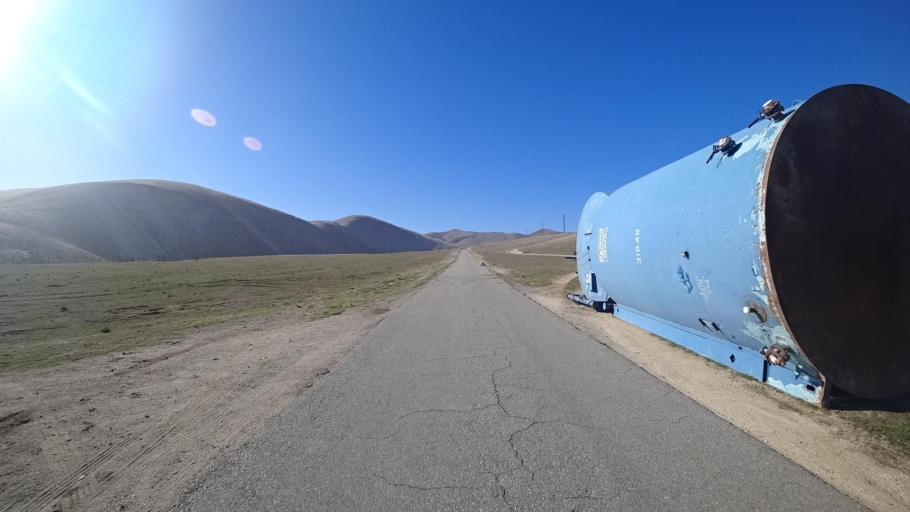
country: US
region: California
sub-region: Kern County
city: Taft Heights
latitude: 35.2321
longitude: -119.6613
